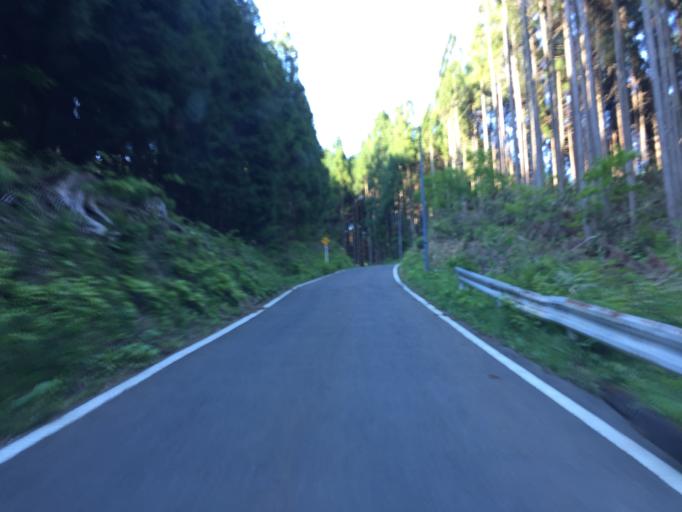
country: JP
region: Ibaraki
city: Kitaibaraki
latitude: 36.9014
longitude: 140.5935
